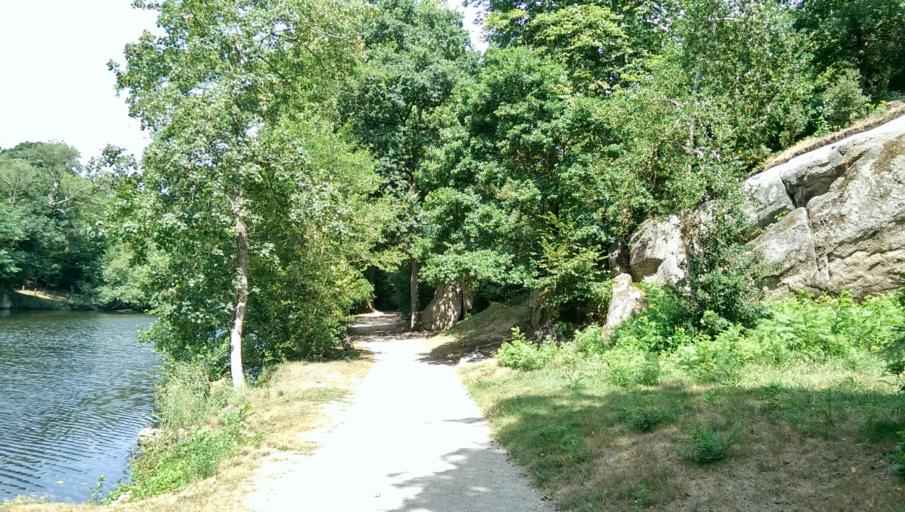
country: FR
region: Pays de la Loire
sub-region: Departement de la Loire-Atlantique
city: Clisson
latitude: 47.0842
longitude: -1.2760
